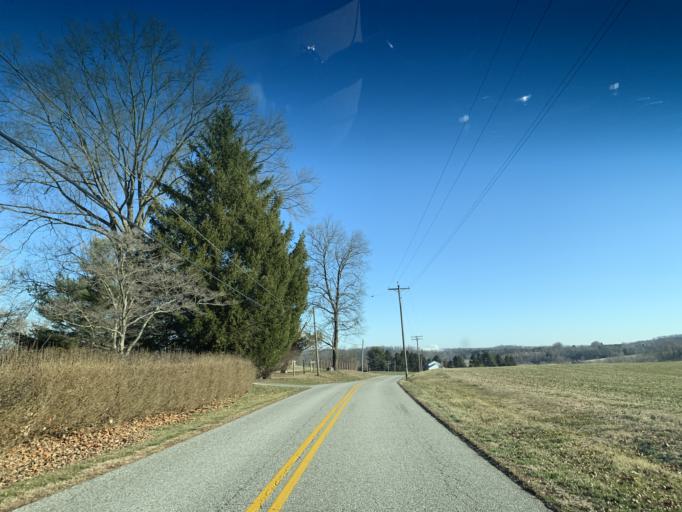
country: US
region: Maryland
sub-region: Harford County
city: Aberdeen
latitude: 39.5802
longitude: -76.2350
